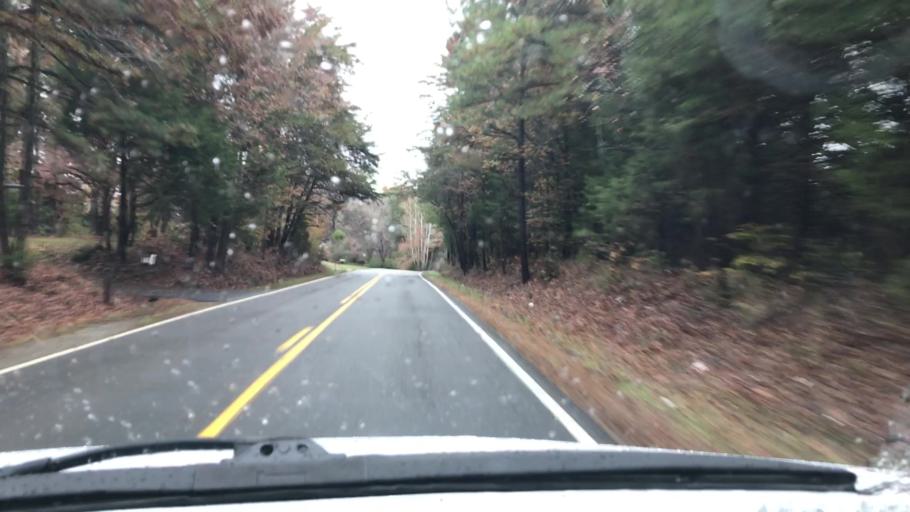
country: US
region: Virginia
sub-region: Henrico County
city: Short Pump
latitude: 37.6291
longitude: -77.6870
